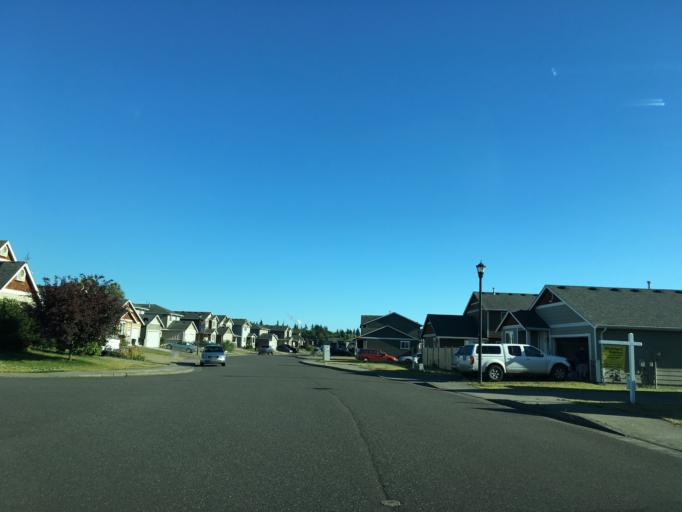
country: US
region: Washington
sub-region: Whatcom County
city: Birch Bay
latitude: 48.9106
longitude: -122.7416
